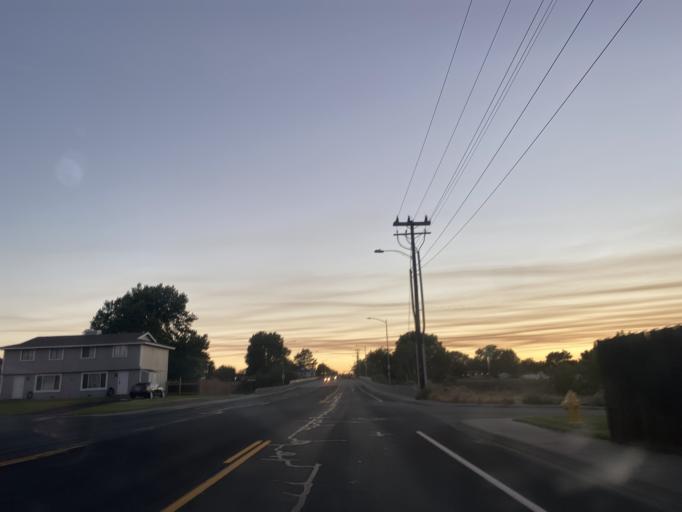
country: US
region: Washington
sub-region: Benton County
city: Kennewick
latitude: 46.1986
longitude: -119.1512
